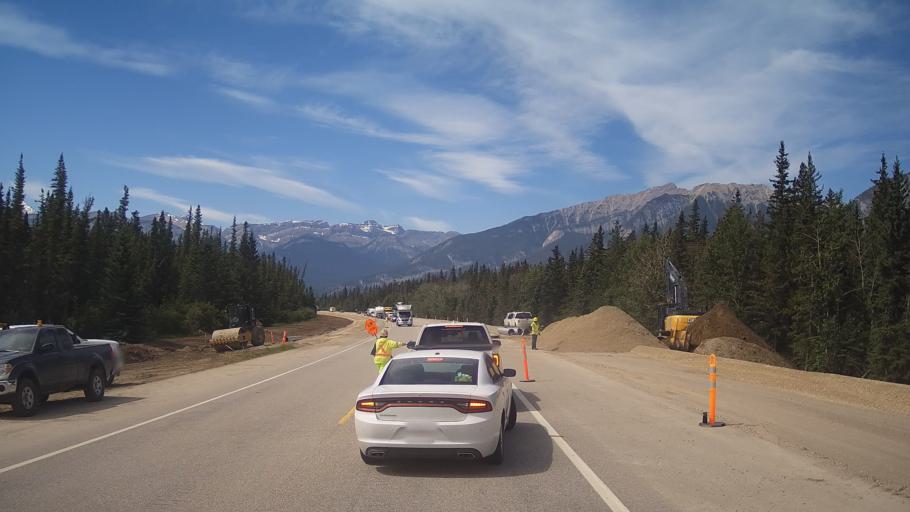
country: CA
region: Alberta
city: Jasper Park Lodge
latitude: 53.0703
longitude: -118.0552
